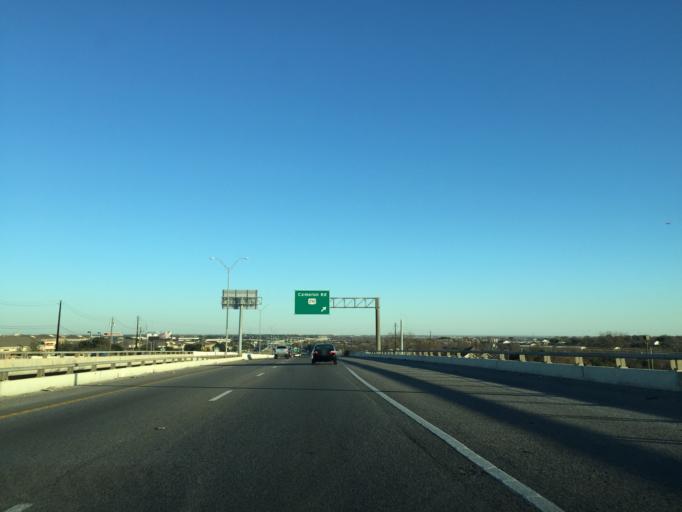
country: US
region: Texas
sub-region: Travis County
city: Austin
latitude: 30.3380
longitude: -97.6982
